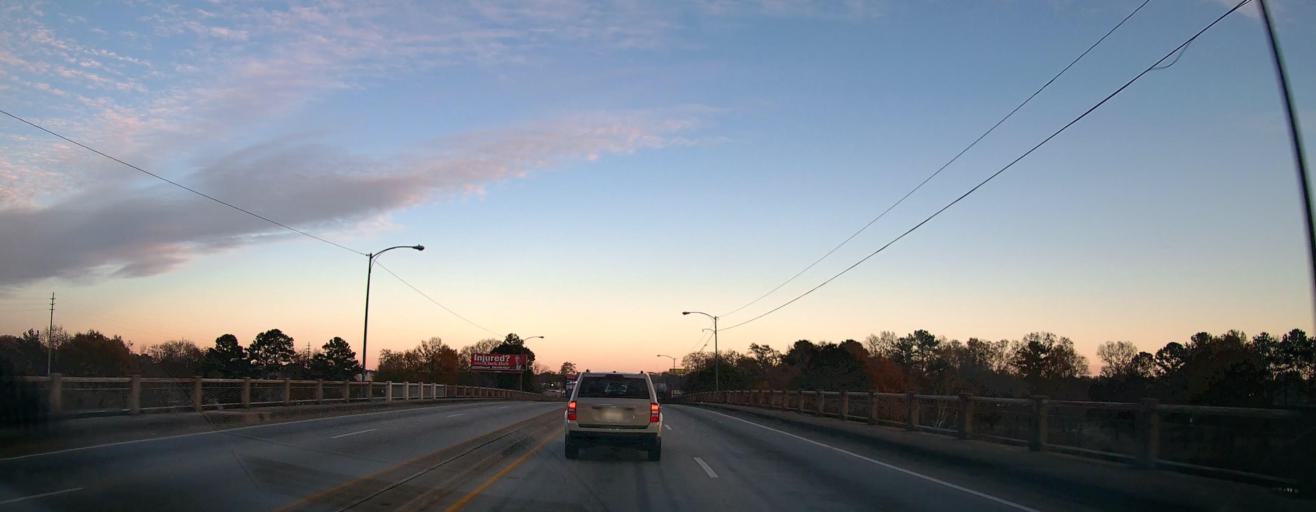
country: US
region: Alabama
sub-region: Etowah County
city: Gadsden
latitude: 34.0128
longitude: -85.9954
